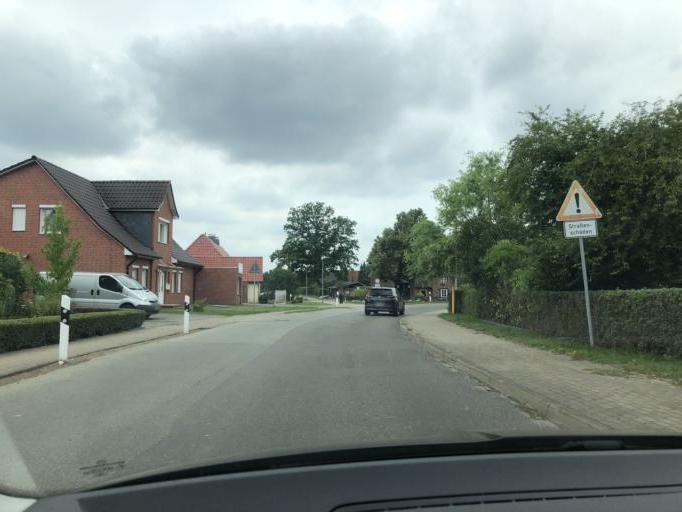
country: DE
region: Mecklenburg-Vorpommern
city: Klein Rogahn
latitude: 53.5695
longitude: 11.3542
